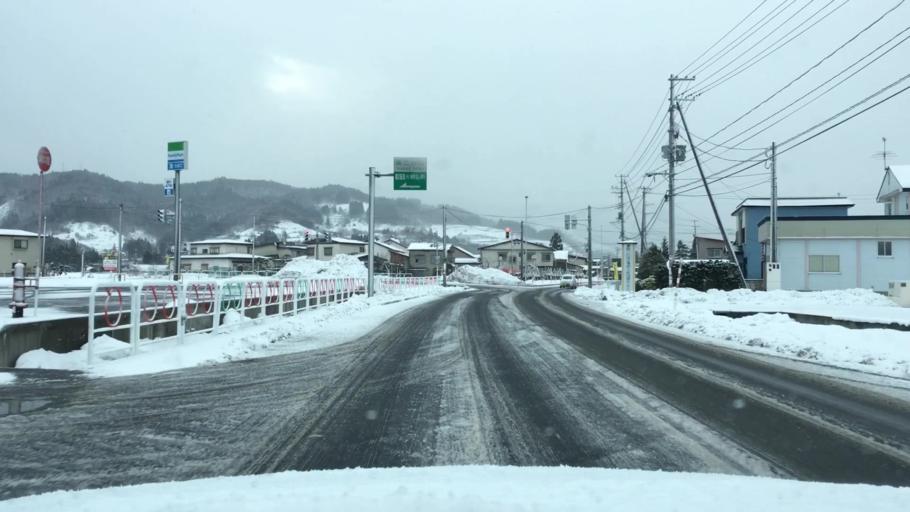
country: JP
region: Aomori
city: Hirosaki
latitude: 40.5469
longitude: 140.5517
